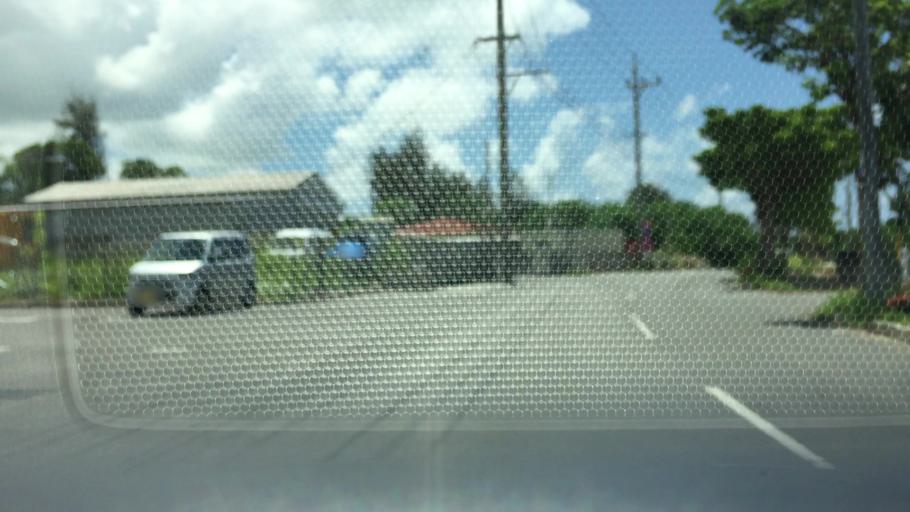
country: JP
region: Okinawa
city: Ishigaki
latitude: 24.3619
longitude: 124.1180
